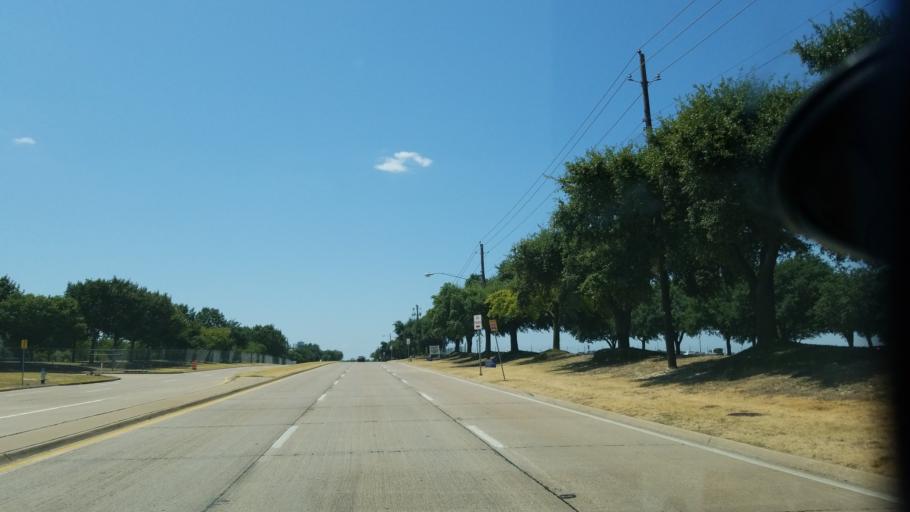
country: US
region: Texas
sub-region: Dallas County
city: Cockrell Hill
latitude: 32.7056
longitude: -96.9127
